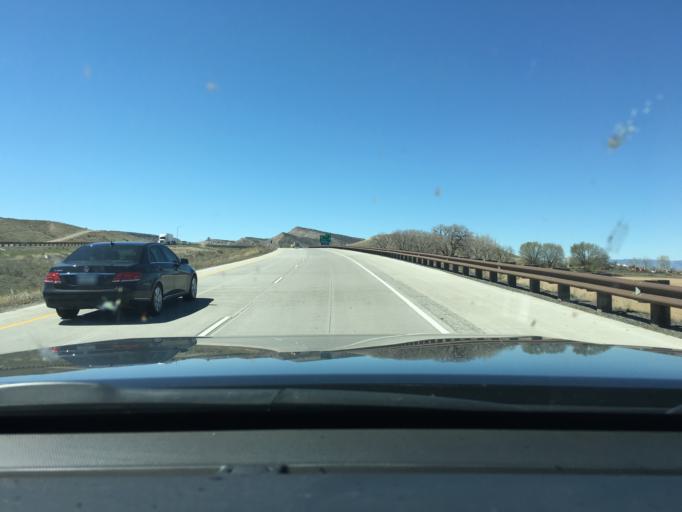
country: US
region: Colorado
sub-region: Mesa County
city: Loma
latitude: 39.1776
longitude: -108.8054
